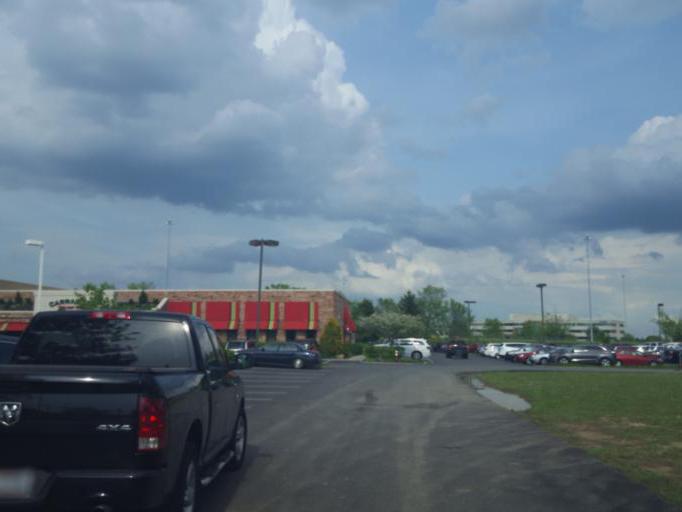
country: US
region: Ohio
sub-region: Franklin County
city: Westerville
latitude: 40.1408
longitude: -82.9741
